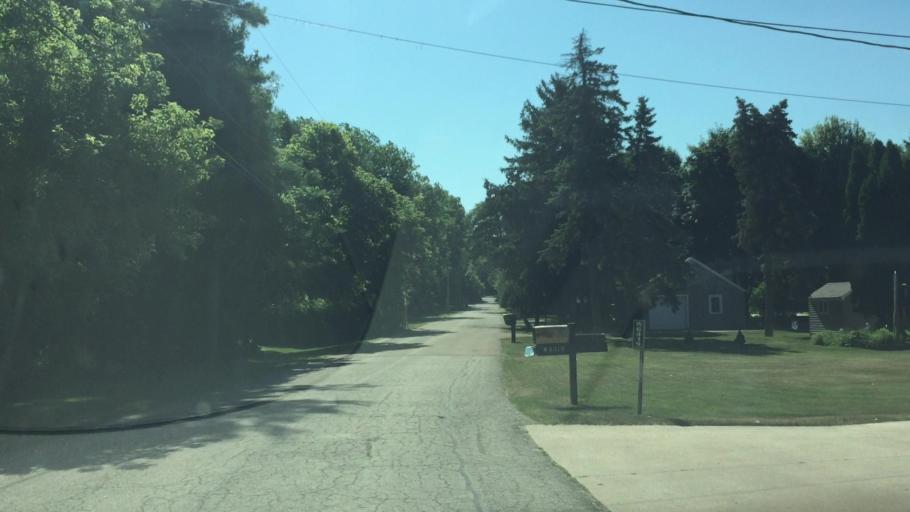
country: US
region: Wisconsin
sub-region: Outagamie County
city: Kimberly
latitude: 44.2043
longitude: -88.3599
